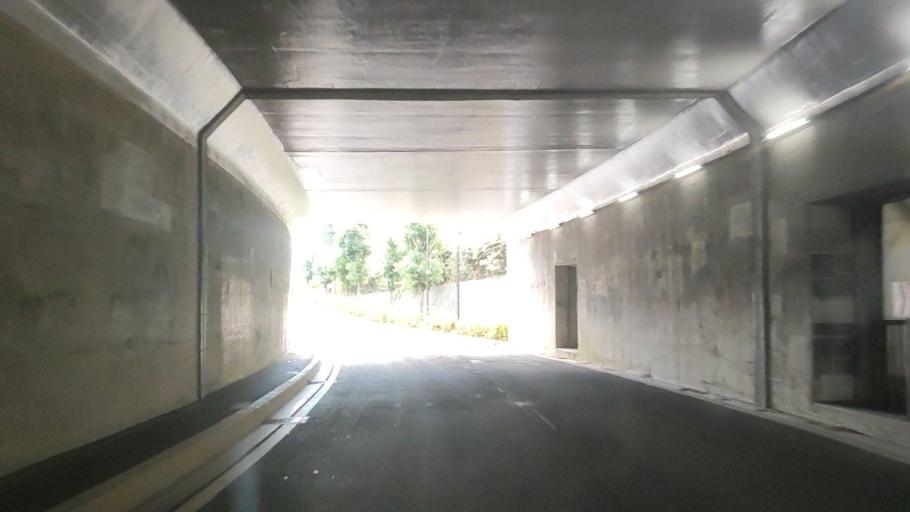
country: JP
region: Kanagawa
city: Yokohama
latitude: 35.4457
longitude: 139.5499
